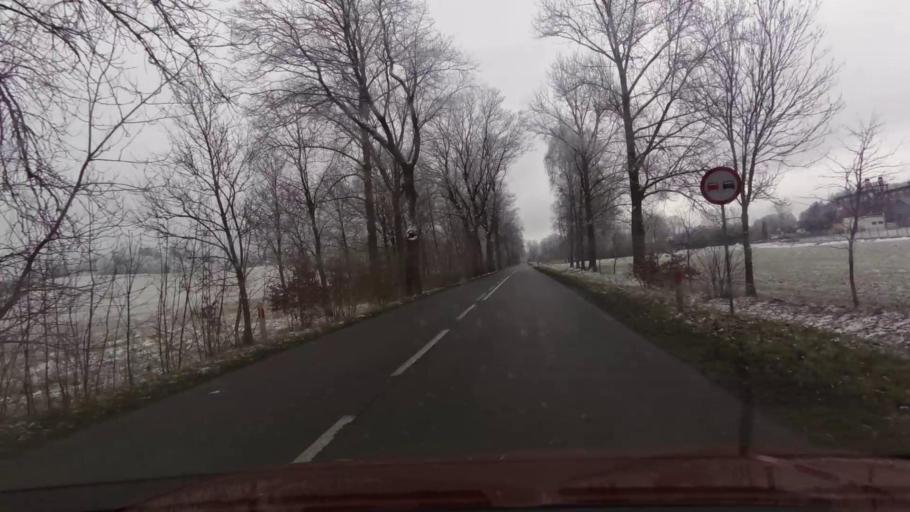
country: PL
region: West Pomeranian Voivodeship
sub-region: Powiat swidwinski
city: Polczyn-Zdroj
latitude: 53.7921
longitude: 16.0334
